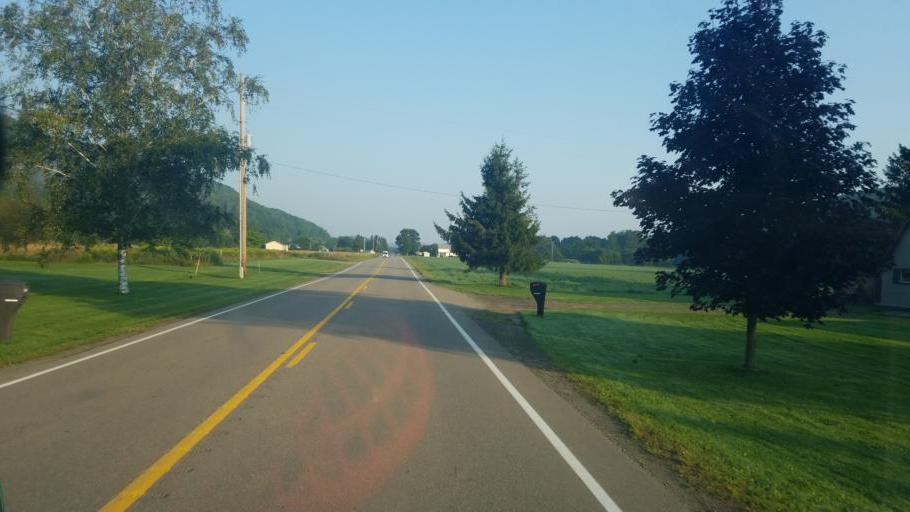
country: US
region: Pennsylvania
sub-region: Tioga County
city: Westfield
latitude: 41.9684
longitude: -77.4527
